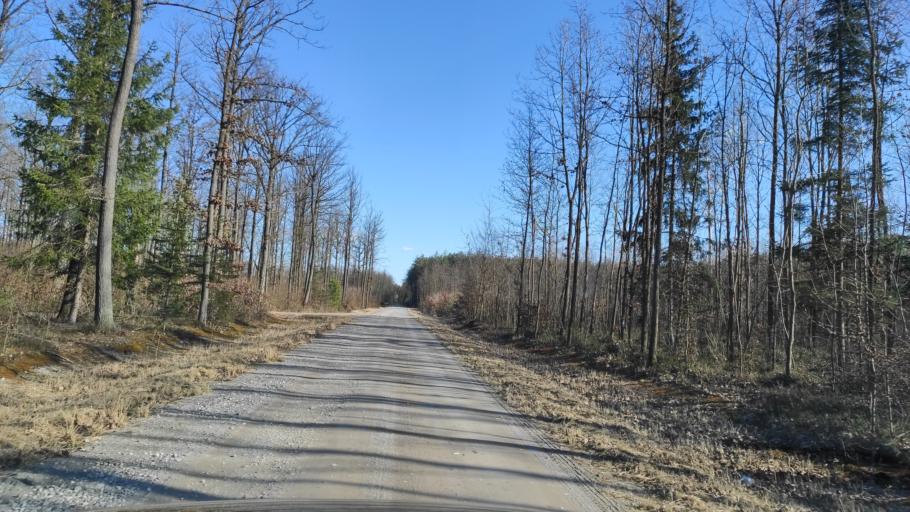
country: PL
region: Masovian Voivodeship
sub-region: Powiat radomski
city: Jedlnia-Letnisko
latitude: 51.4514
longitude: 21.2858
